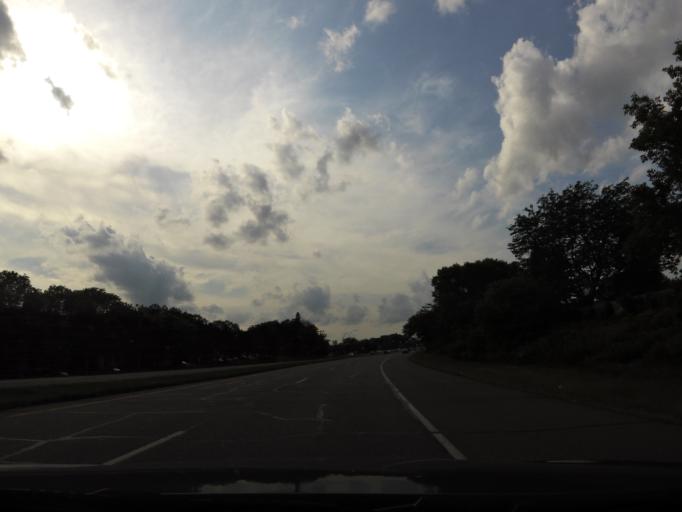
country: US
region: Minnesota
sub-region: Dakota County
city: Burnsville
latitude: 44.7387
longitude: -93.2650
